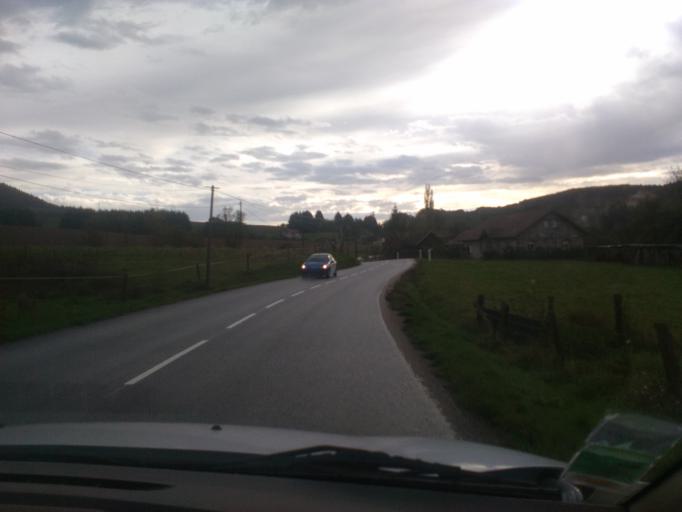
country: FR
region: Lorraine
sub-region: Departement des Vosges
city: Granges-sur-Vologne
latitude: 48.1805
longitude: 6.8129
